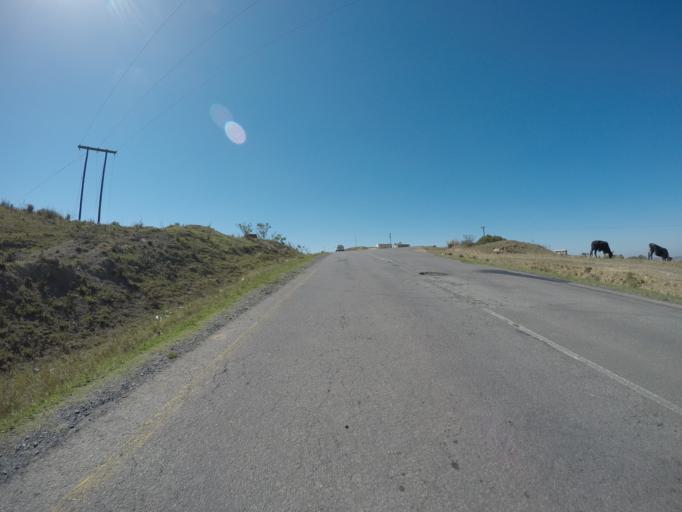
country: ZA
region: Eastern Cape
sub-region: OR Tambo District Municipality
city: Mthatha
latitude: -31.9106
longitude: 28.9548
